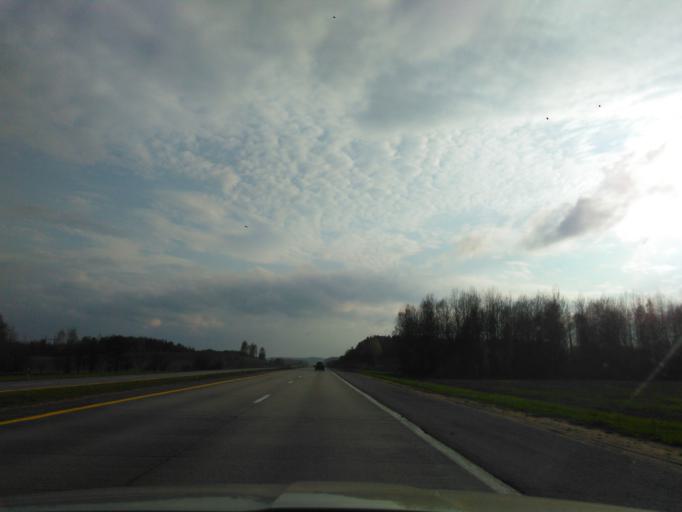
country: BY
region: Minsk
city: Astrashytski Haradok
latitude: 54.0860
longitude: 27.7577
